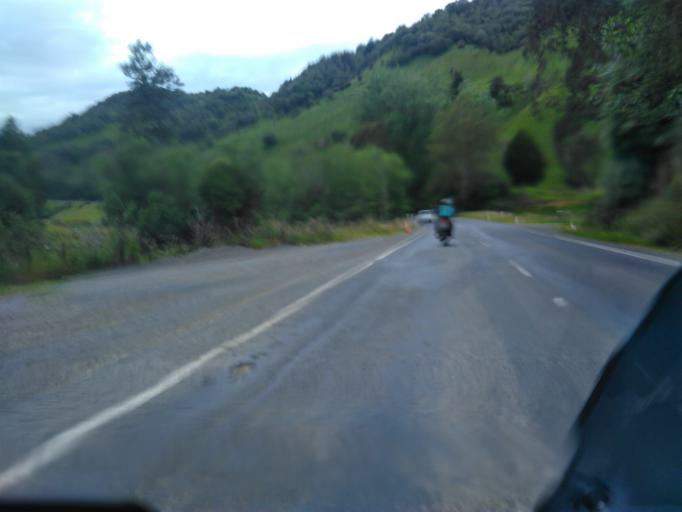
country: NZ
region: Bay of Plenty
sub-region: Opotiki District
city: Opotiki
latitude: -38.3751
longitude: 177.4853
